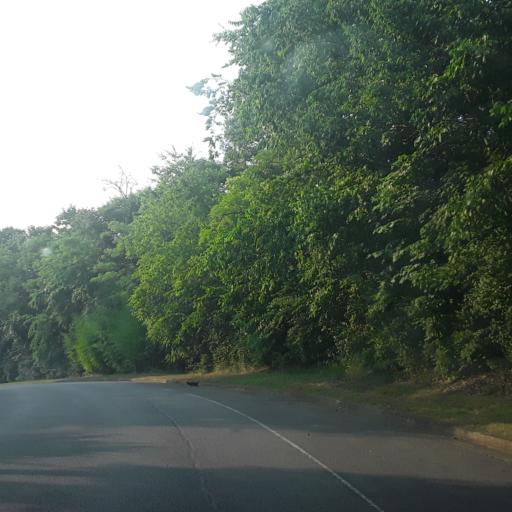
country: US
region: Tennessee
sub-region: Williamson County
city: Brentwood Estates
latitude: 36.0391
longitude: -86.7241
